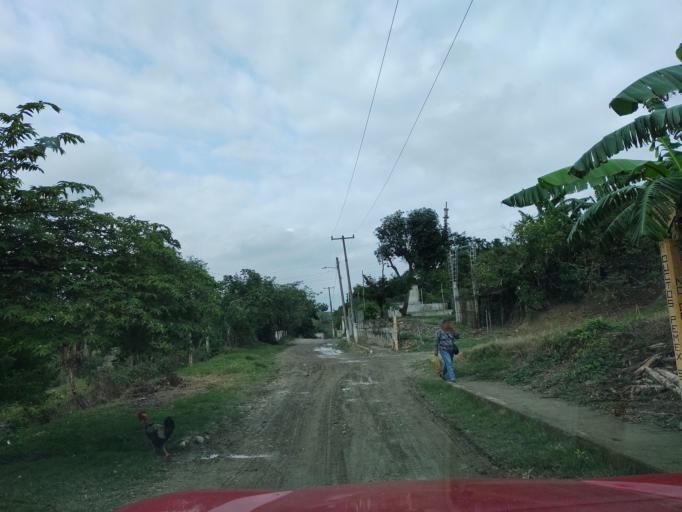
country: MX
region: Veracruz
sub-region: Papantla
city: El Chote
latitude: 20.4405
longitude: -97.4071
